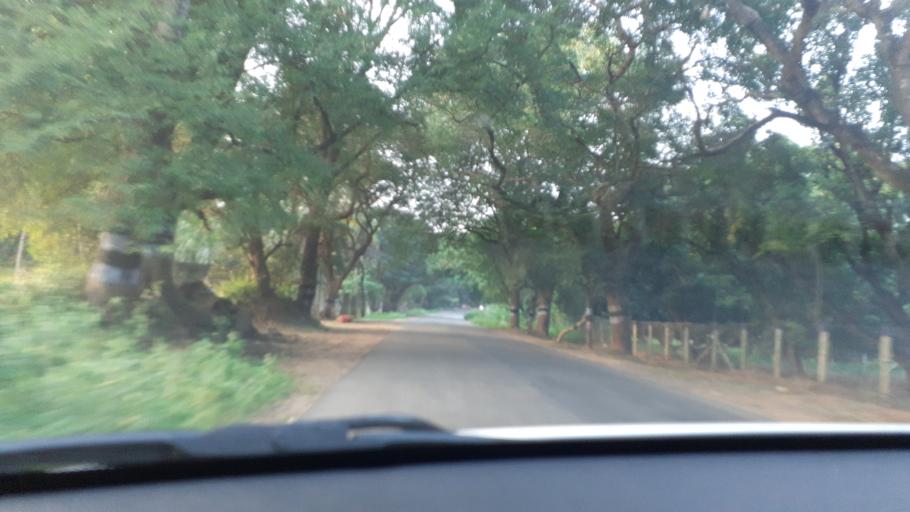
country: IN
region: Tamil Nadu
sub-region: Dindigul
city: Ayakudi
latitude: 10.4042
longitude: 77.5447
